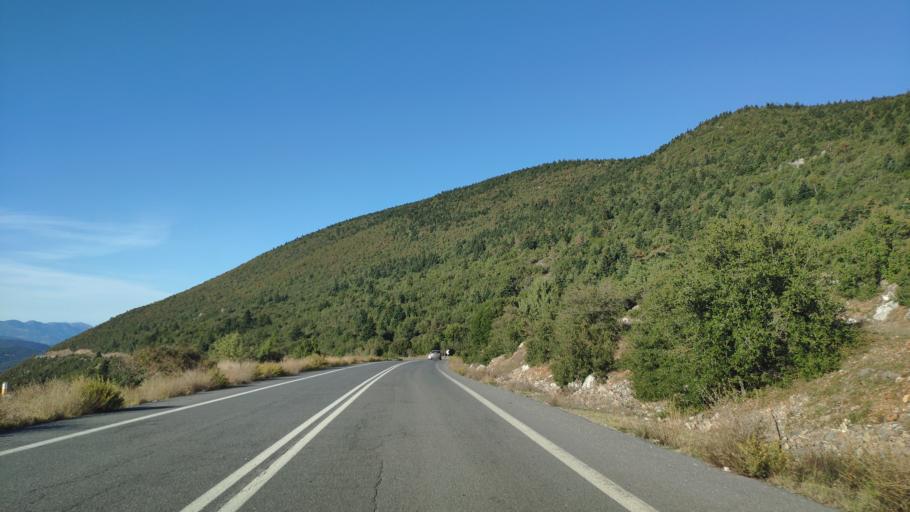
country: GR
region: Peloponnese
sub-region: Nomos Arkadias
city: Langadhia
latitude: 37.6963
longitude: 22.1986
